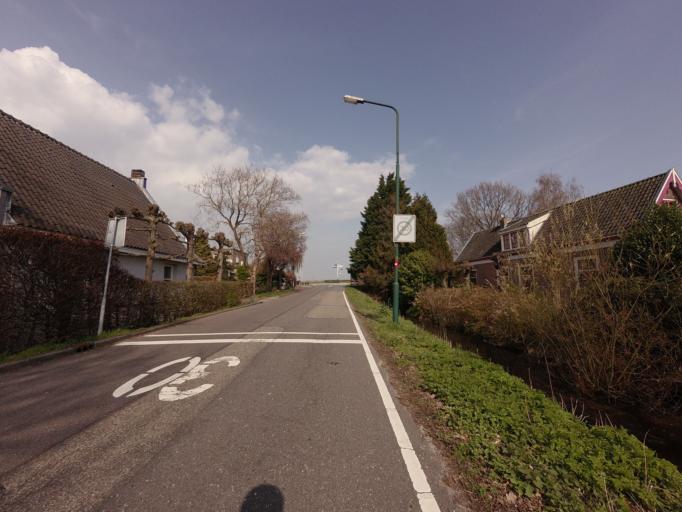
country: NL
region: North Holland
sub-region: Gemeente Wijdemeren
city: Kortenhoef
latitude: 52.2749
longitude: 5.1078
